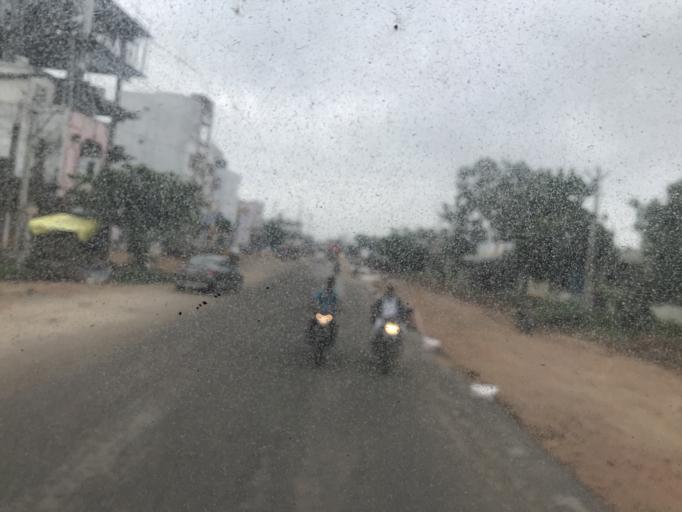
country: IN
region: Telangana
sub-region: Mahbubnagar
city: Mahbubnagar
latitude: 16.7740
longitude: 78.1267
